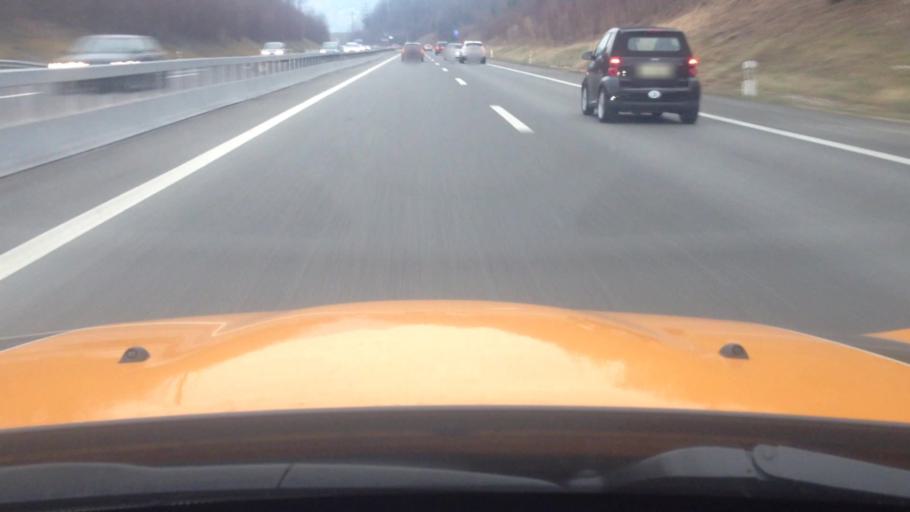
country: CH
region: Ticino
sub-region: Mendrisio District
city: Novazzano
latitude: 45.8523
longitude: 8.9819
